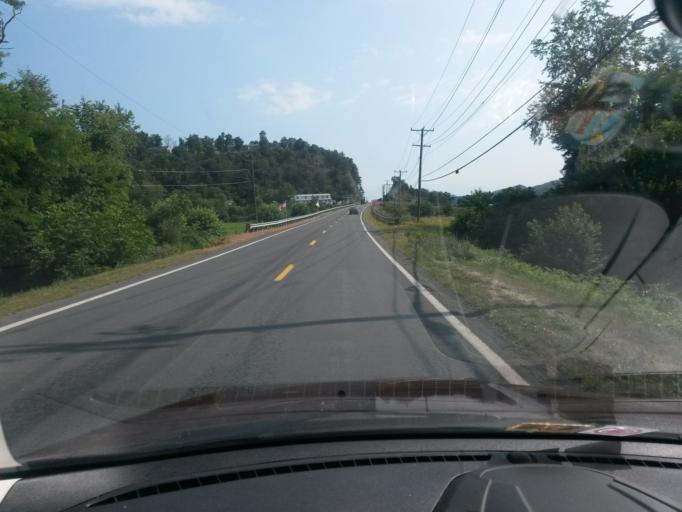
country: US
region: Virginia
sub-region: Shenandoah County
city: Basye
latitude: 38.8823
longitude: -78.8639
